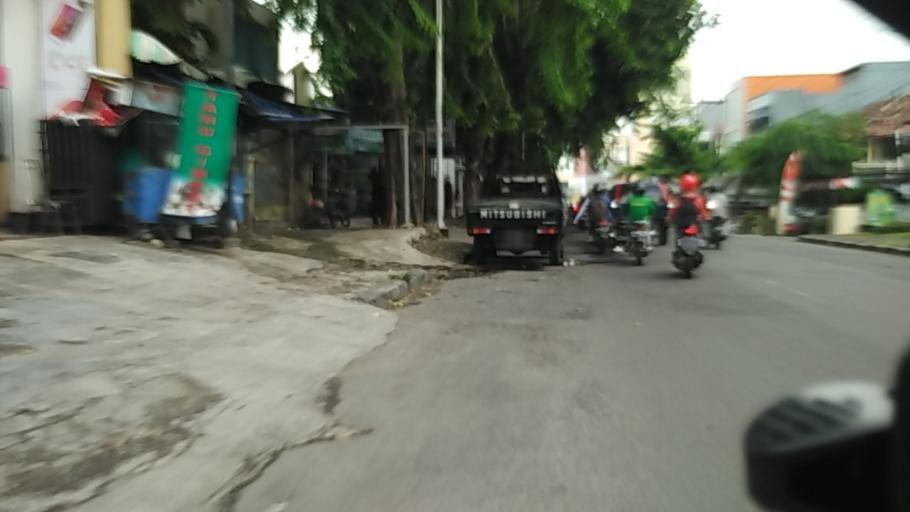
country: ID
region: Central Java
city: Semarang
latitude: -7.0049
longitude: 110.4295
